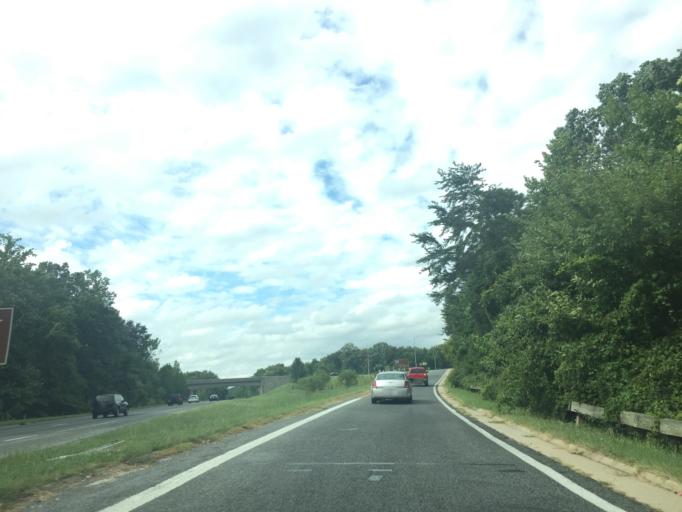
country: US
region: Maryland
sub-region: Anne Arundel County
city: Maryland City
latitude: 39.0985
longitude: -76.8004
